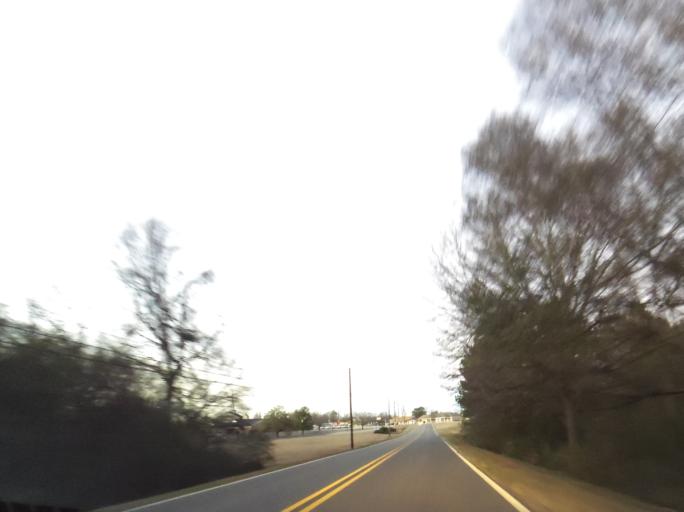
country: US
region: Georgia
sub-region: Peach County
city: Byron
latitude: 32.6464
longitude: -83.7573
